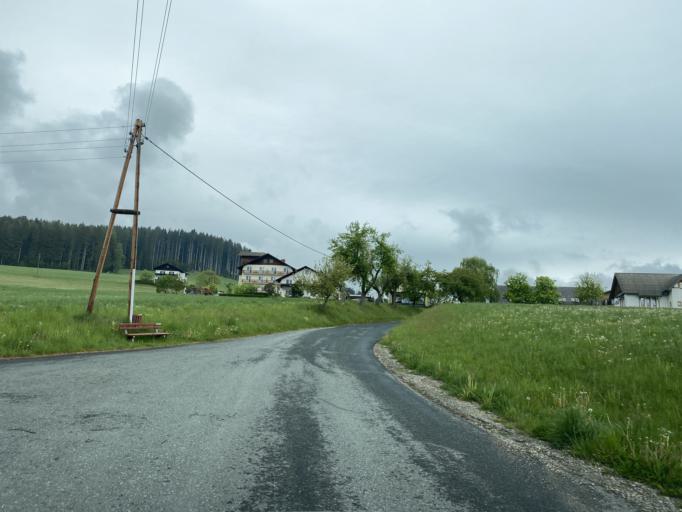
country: AT
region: Styria
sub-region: Politischer Bezirk Weiz
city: Strallegg
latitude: 47.3928
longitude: 15.6834
